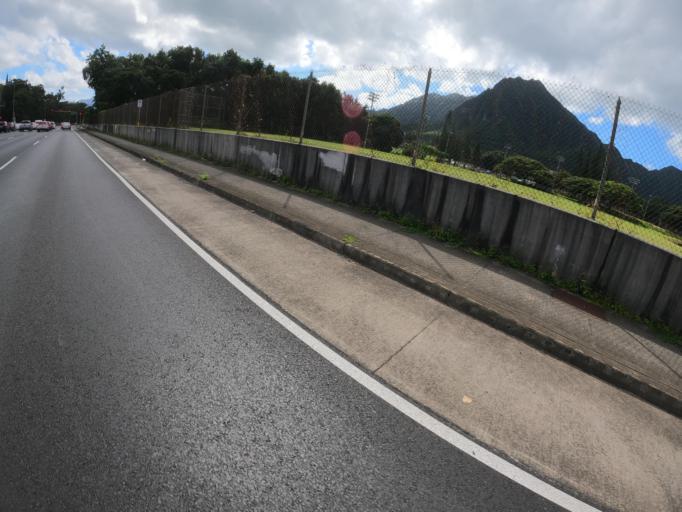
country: US
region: Hawaii
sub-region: Honolulu County
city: Kane'ohe
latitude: 21.4115
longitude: -157.8090
